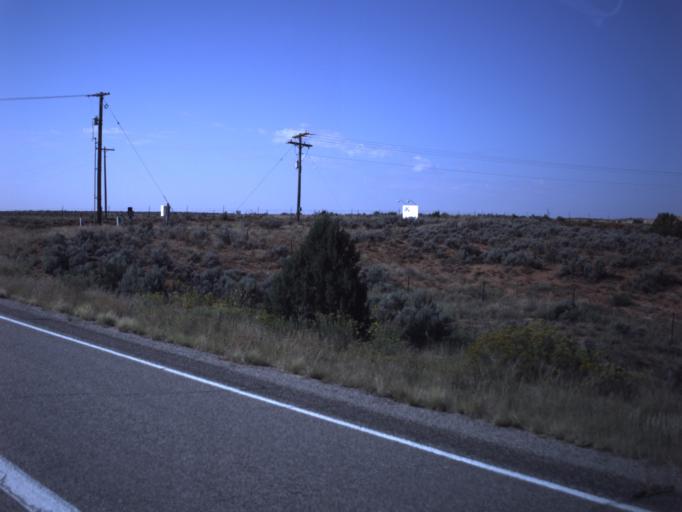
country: US
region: Utah
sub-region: San Juan County
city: Blanding
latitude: 37.5347
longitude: -109.4942
